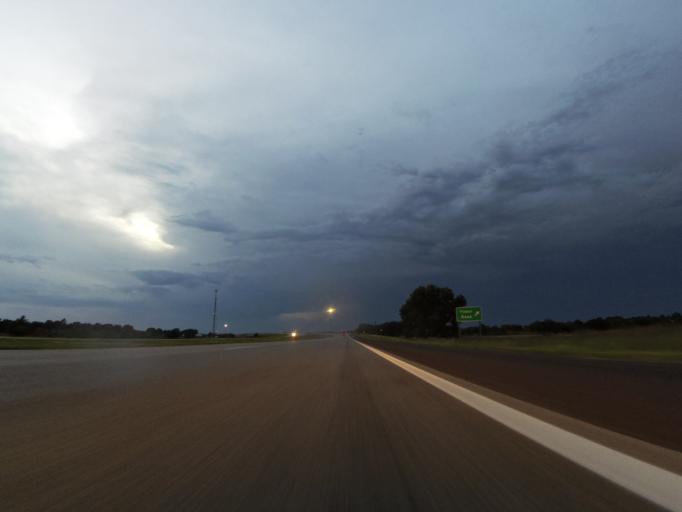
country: US
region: Kansas
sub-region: Reno County
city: Haven
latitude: 37.9341
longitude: -97.8582
